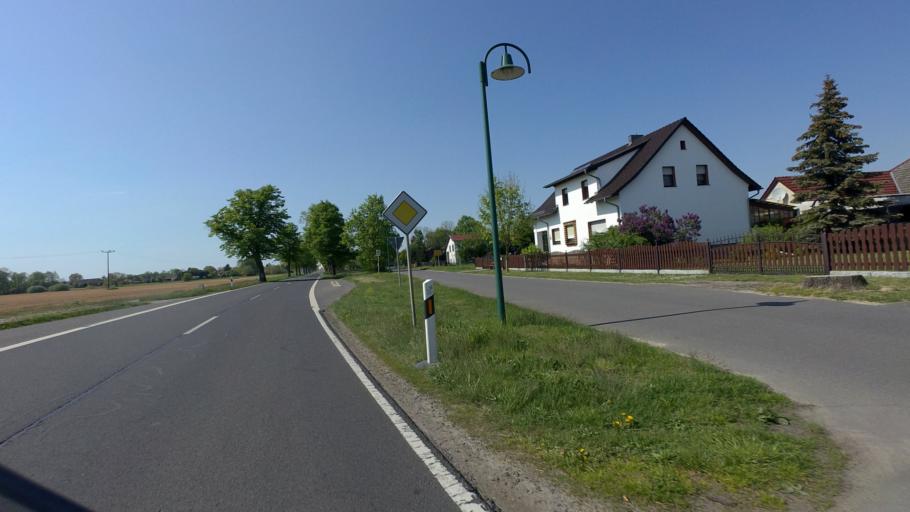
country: DE
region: Brandenburg
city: Schlepzig
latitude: 52.0556
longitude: 13.9659
